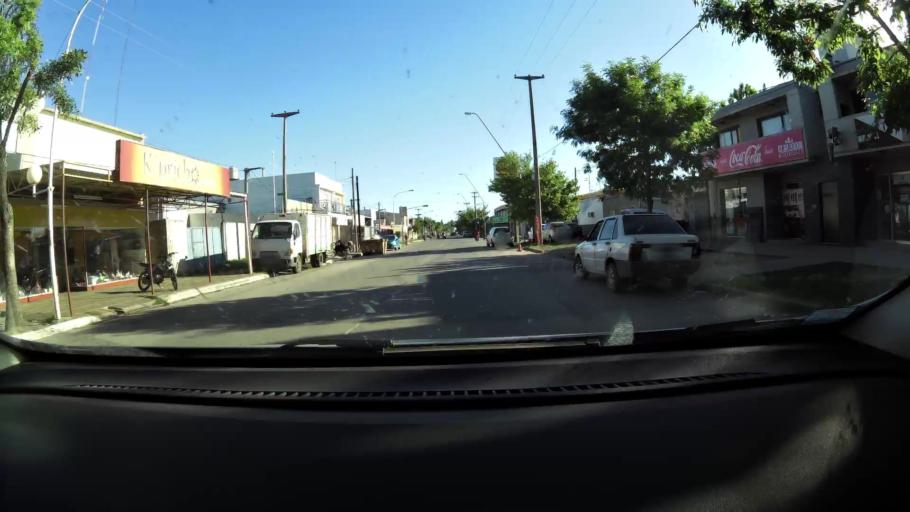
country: AR
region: Cordoba
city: San Francisco
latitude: -31.4378
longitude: -62.0683
